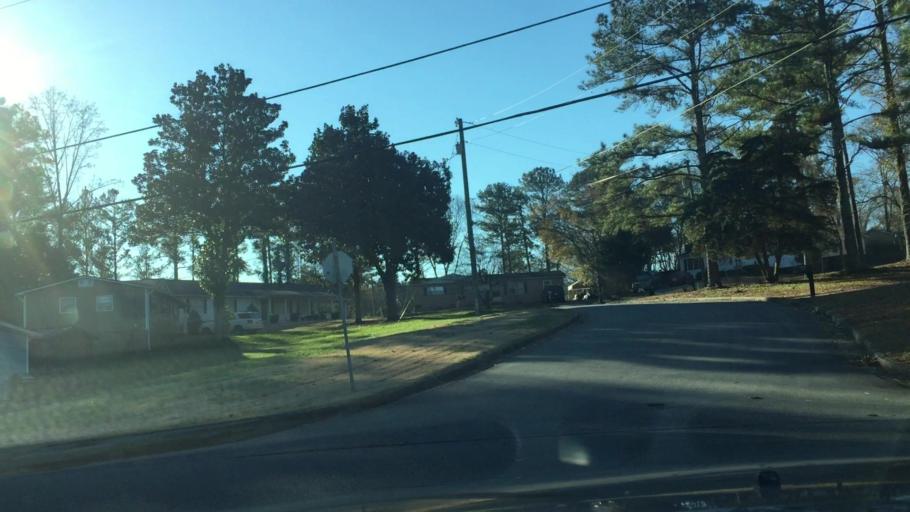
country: US
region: Georgia
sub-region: Cherokee County
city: Woodstock
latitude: 34.0650
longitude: -84.5251
